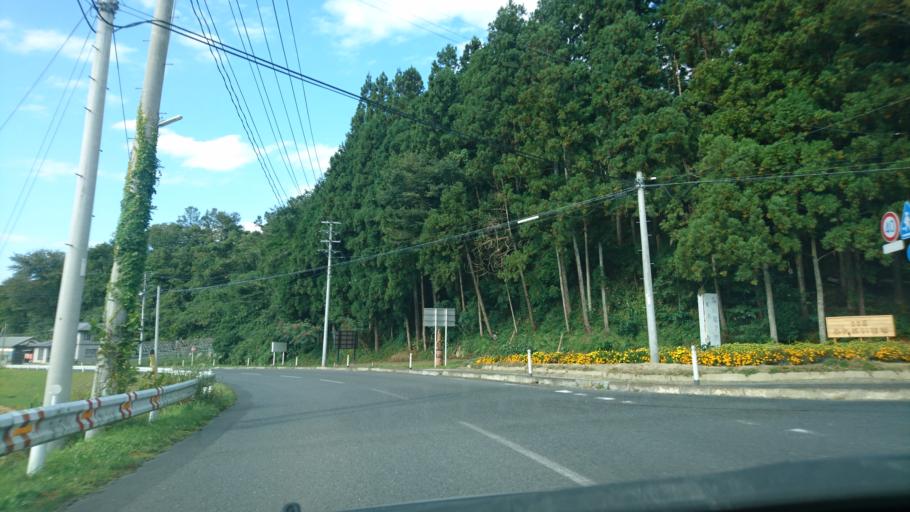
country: JP
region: Iwate
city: Ichinoseki
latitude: 38.8918
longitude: 141.3326
